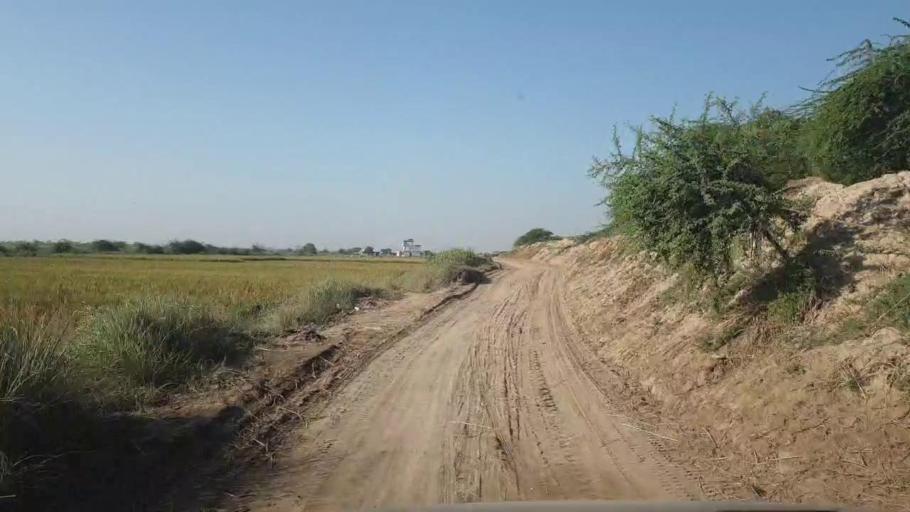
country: PK
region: Sindh
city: Badin
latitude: 24.7110
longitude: 68.7844
